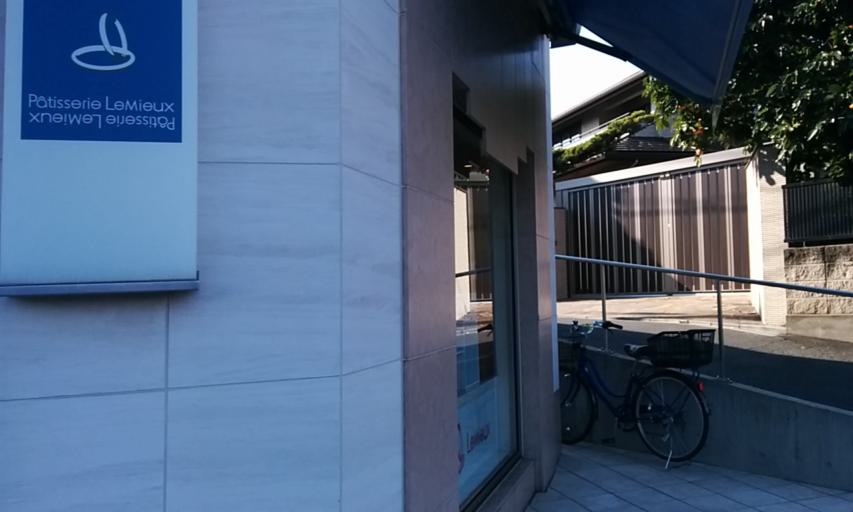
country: JP
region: Tokyo
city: Chofugaoka
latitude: 35.6576
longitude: 139.5755
